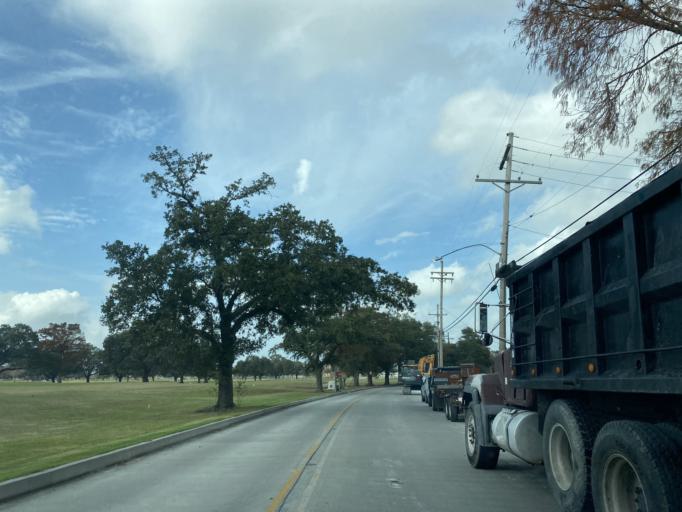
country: US
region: Louisiana
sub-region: Saint Bernard Parish
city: Arabi
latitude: 30.0232
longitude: -90.0382
